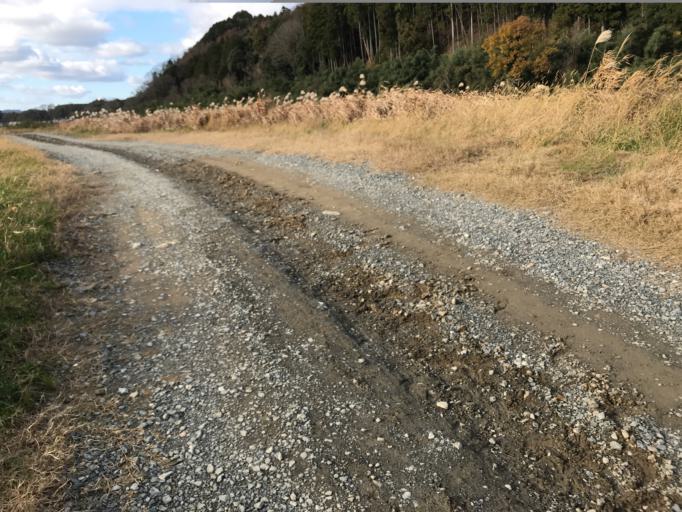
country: JP
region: Kyoto
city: Kameoka
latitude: 35.0147
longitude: 135.6052
